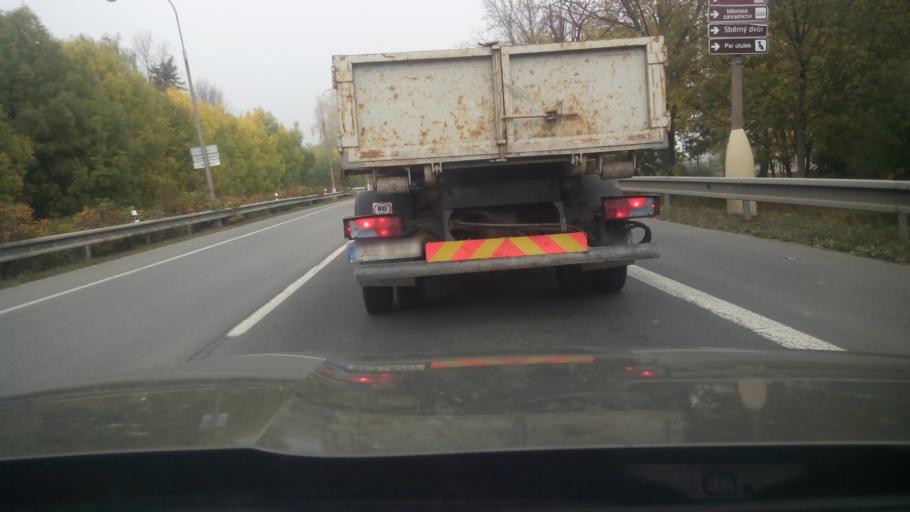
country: CZ
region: Jihocesky
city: Strakonice
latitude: 49.2618
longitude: 13.9149
